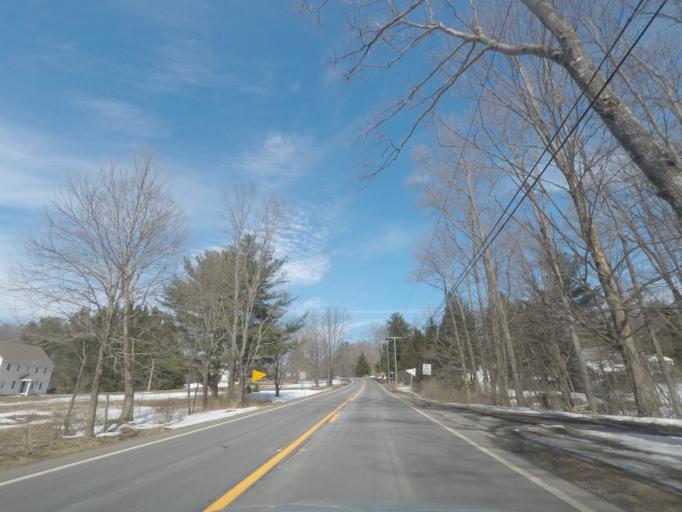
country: US
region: Massachusetts
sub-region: Berkshire County
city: West Stockbridge
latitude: 42.3554
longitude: -73.3816
